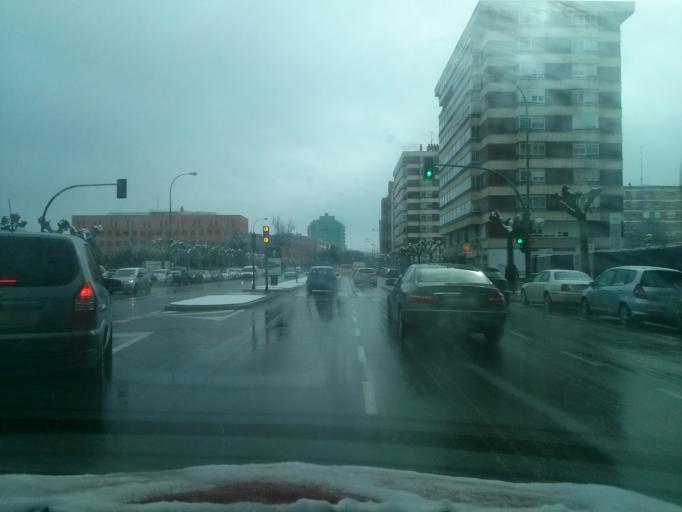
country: ES
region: Castille and Leon
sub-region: Provincia de Burgos
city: Burgos
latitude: 42.3489
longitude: -3.6886
